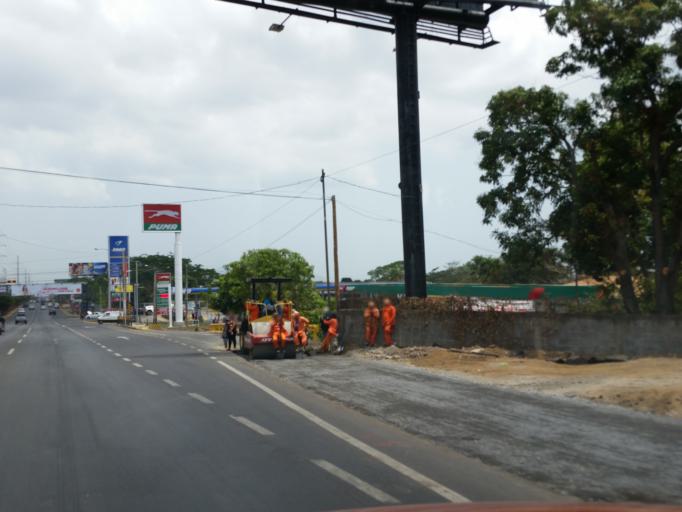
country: NI
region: Managua
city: Managua
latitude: 12.0970
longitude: -86.2403
